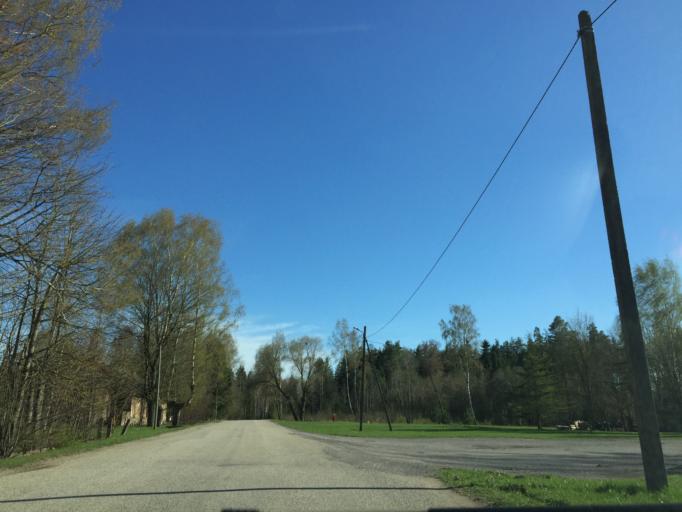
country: EE
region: Valgamaa
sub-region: Valga linn
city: Valga
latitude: 57.8656
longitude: 26.2517
